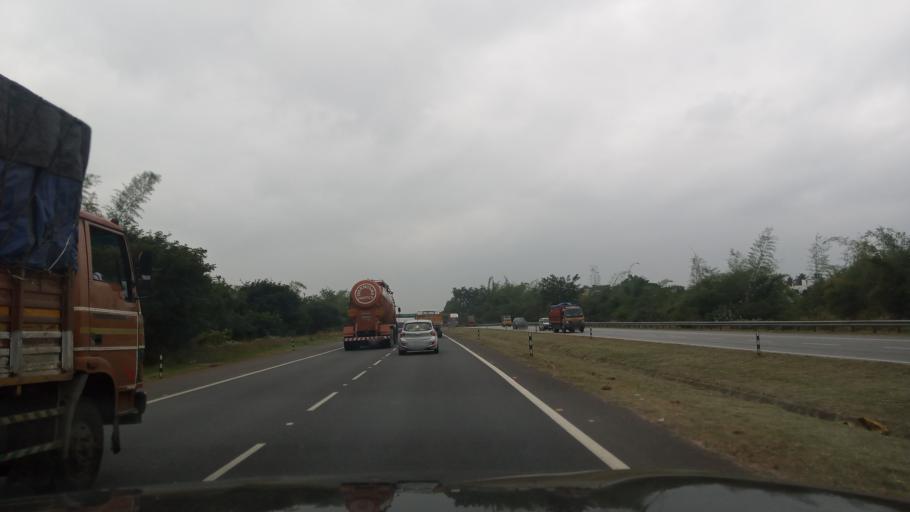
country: IN
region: Karnataka
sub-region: Bangalore Rural
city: Nelamangala
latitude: 13.0296
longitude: 77.4755
